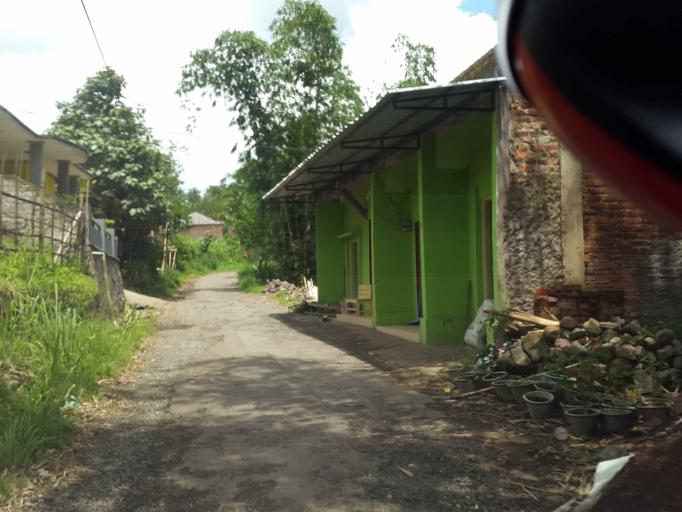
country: ID
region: West Java
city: Sukabumi
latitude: -6.9047
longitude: 106.9443
